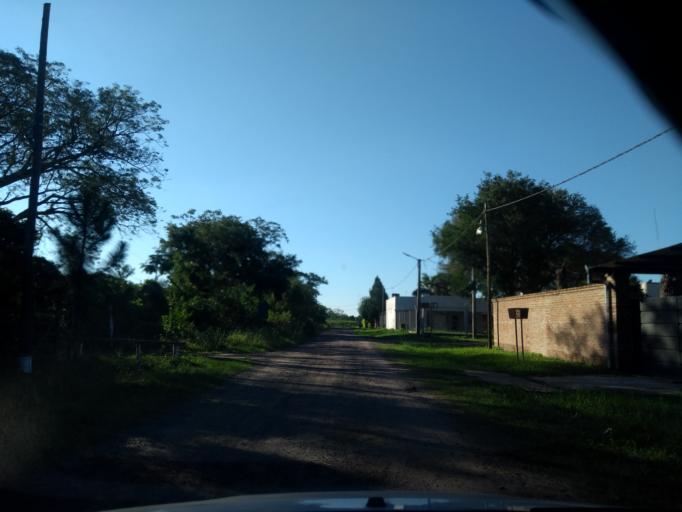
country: AR
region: Chaco
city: Barranqueras
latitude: -27.4385
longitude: -58.9099
